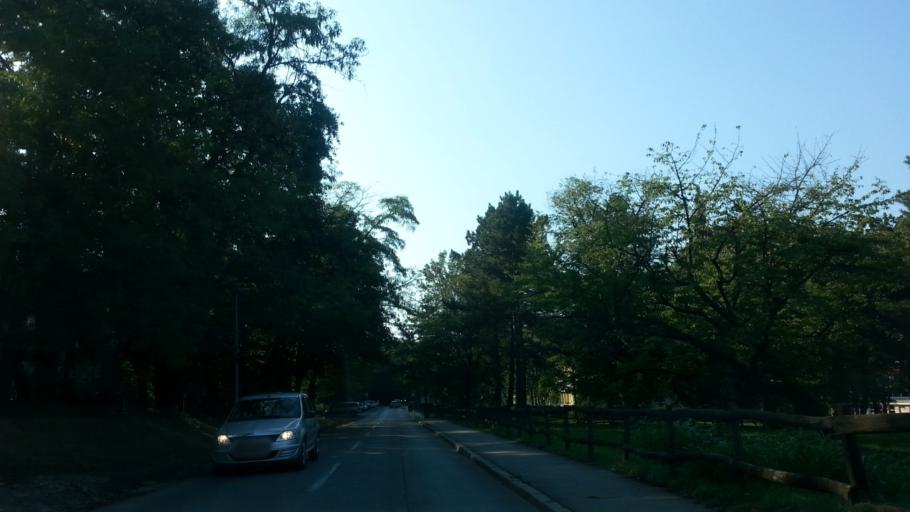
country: RS
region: Central Serbia
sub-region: Belgrade
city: Cukarica
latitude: 44.7660
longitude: 20.4293
